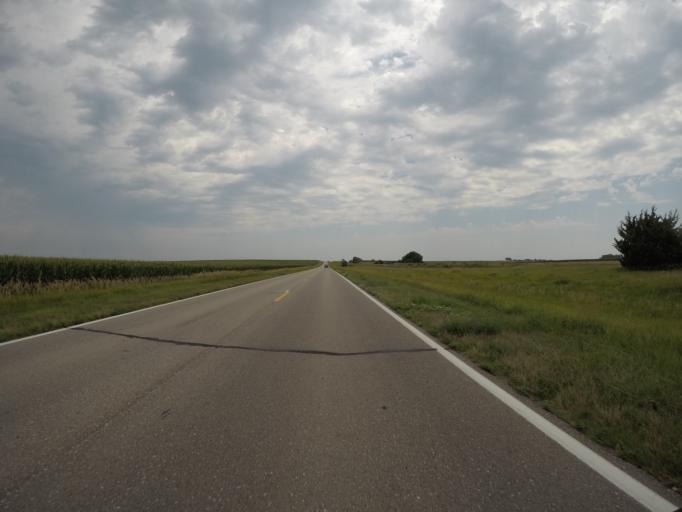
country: US
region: Nebraska
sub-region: Buffalo County
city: Shelton
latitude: 40.6171
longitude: -98.6257
